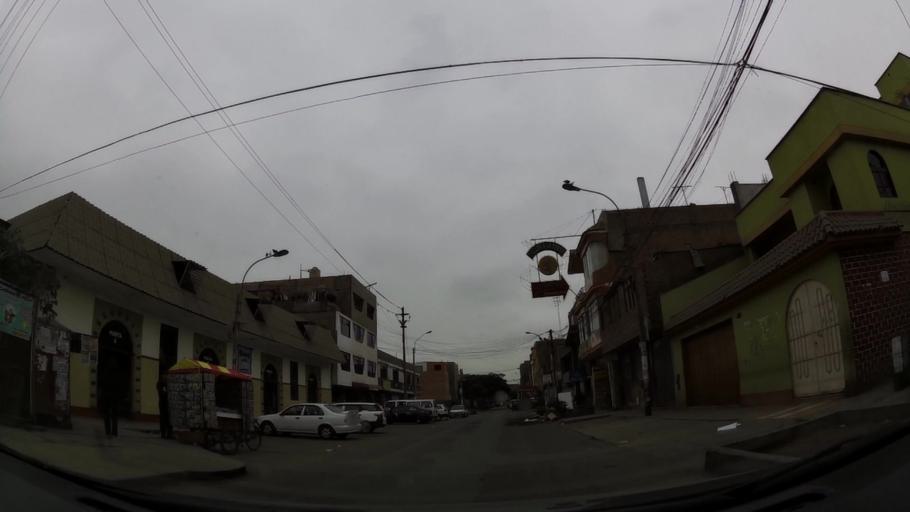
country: PE
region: Lima
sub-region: Lima
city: Independencia
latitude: -11.9658
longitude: -77.0598
